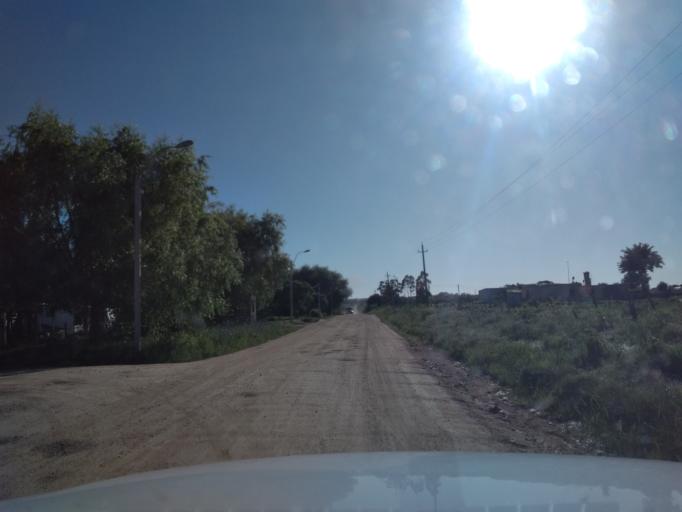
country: UY
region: Canelones
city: Pando
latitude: -34.6959
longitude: -55.9720
